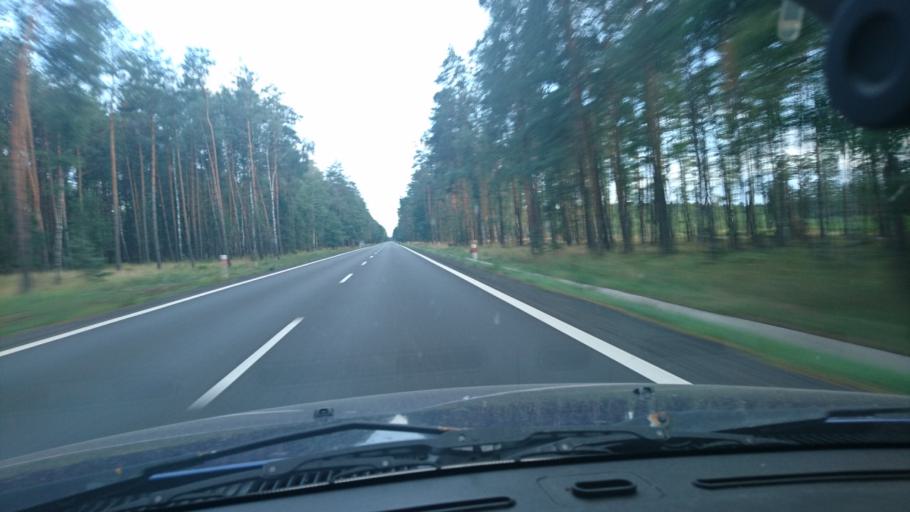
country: PL
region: Silesian Voivodeship
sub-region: Powiat tarnogorski
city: Tworog
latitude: 50.5668
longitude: 18.7119
